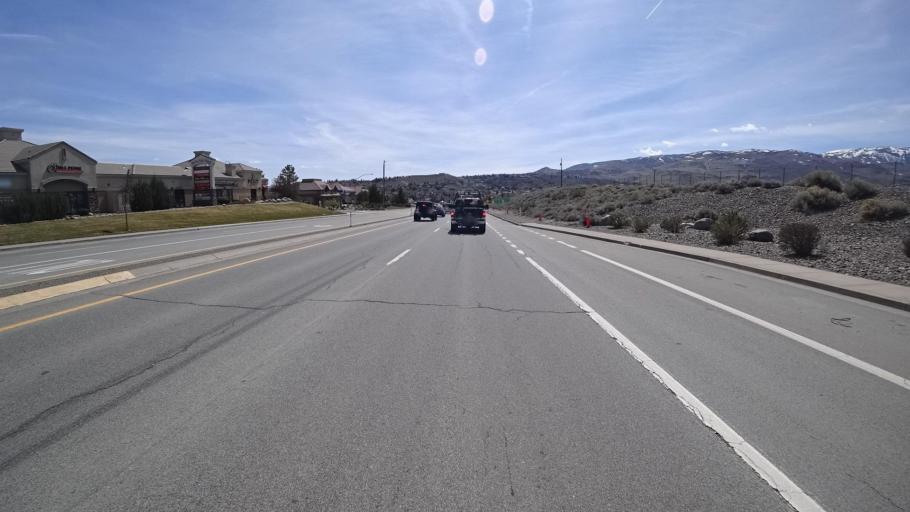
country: US
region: Nevada
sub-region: Washoe County
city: Reno
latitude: 39.5145
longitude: -119.8601
